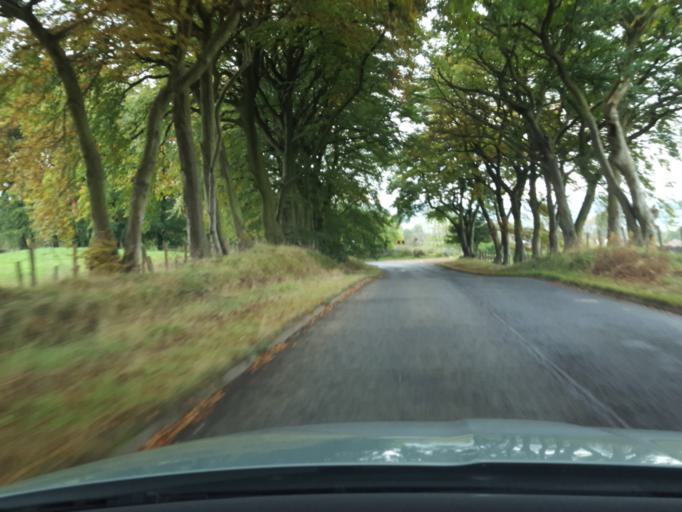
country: GB
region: Scotland
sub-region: West Lothian
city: Bathgate
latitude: 55.9079
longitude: -3.6238
